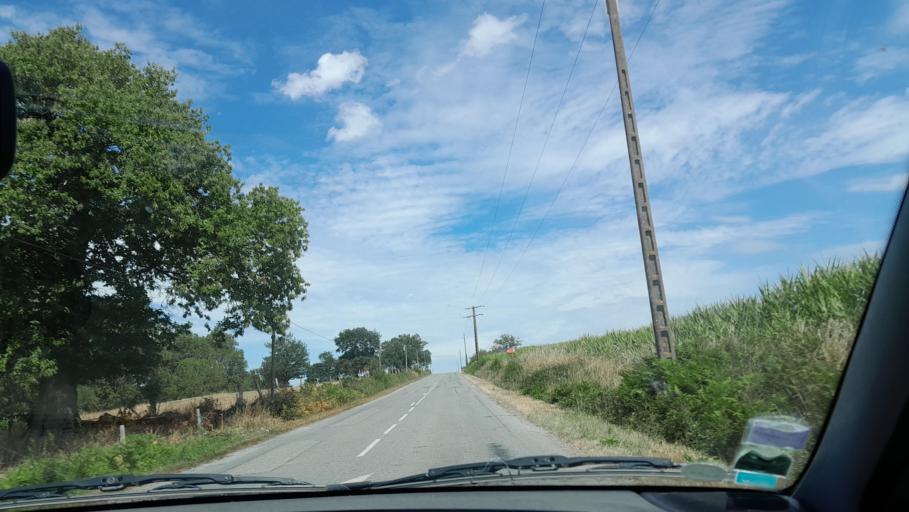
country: FR
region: Brittany
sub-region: Departement d'Ille-et-Vilaine
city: Le Pertre
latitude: 47.9980
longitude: -1.0399
